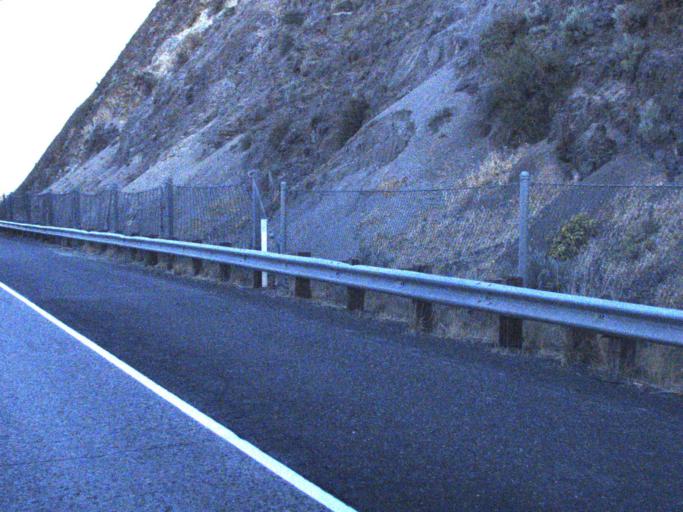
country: US
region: Washington
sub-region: Kittitas County
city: Kittitas
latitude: 46.8801
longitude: -120.4243
